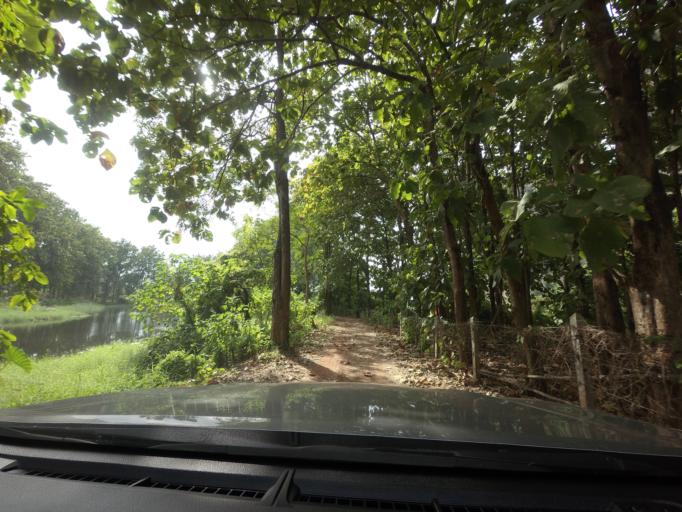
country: TH
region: Phitsanulok
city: Noen Maprang
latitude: 16.5839
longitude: 100.6845
